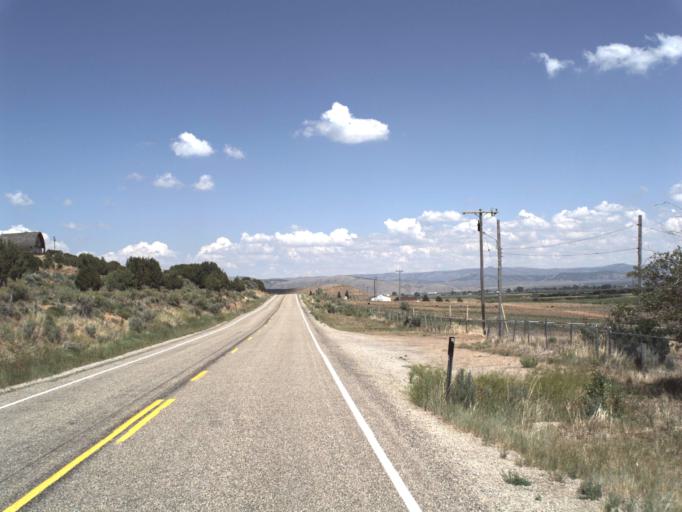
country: US
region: Utah
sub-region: Rich County
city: Randolph
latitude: 41.5116
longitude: -111.2219
